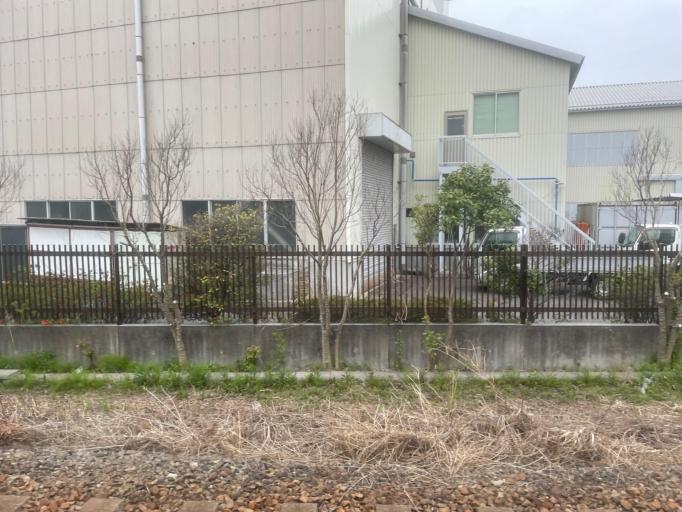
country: JP
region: Kanagawa
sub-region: Kawasaki-shi
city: Kawasaki
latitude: 35.5032
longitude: 139.7085
